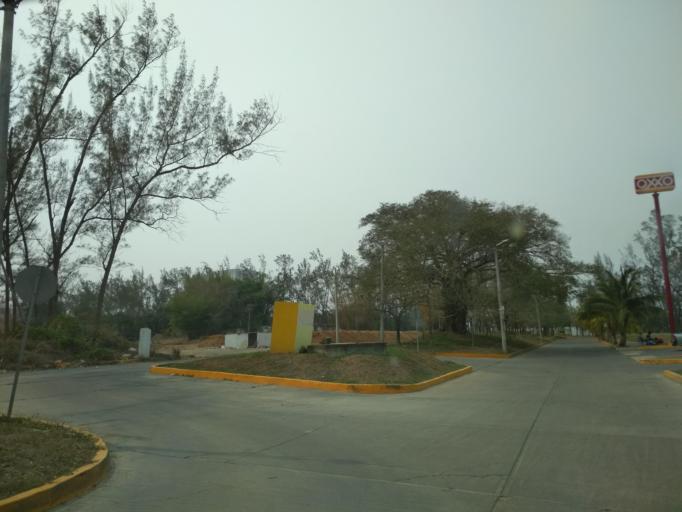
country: MX
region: Veracruz
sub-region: Veracruz
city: Las Amapolas
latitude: 19.1469
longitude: -96.2239
